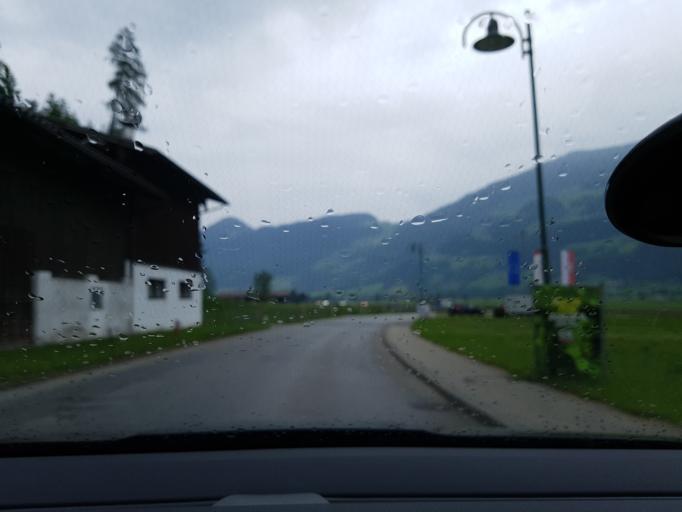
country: AT
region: Tyrol
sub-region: Politischer Bezirk Schwaz
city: Fugen
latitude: 47.3533
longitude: 11.8506
